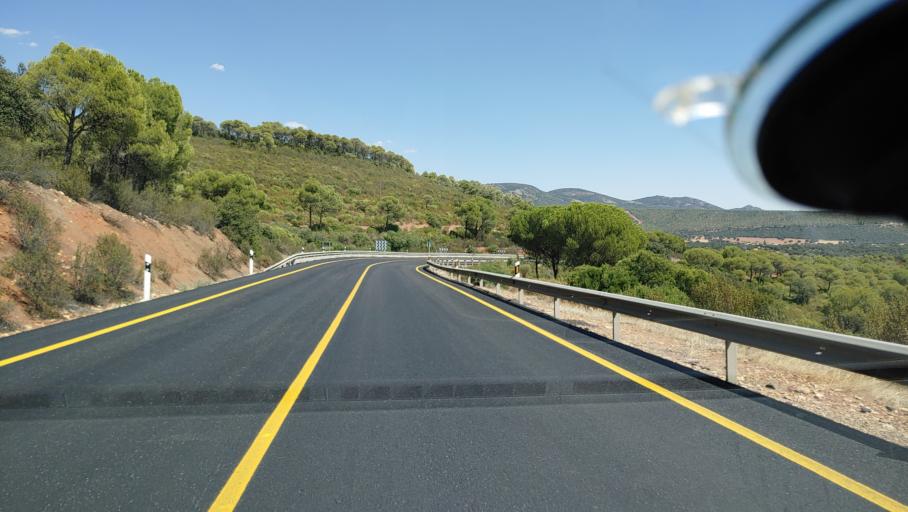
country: ES
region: Castille-La Mancha
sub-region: Provincia de Ciudad Real
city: Abenojar
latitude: 39.0204
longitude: -4.4509
